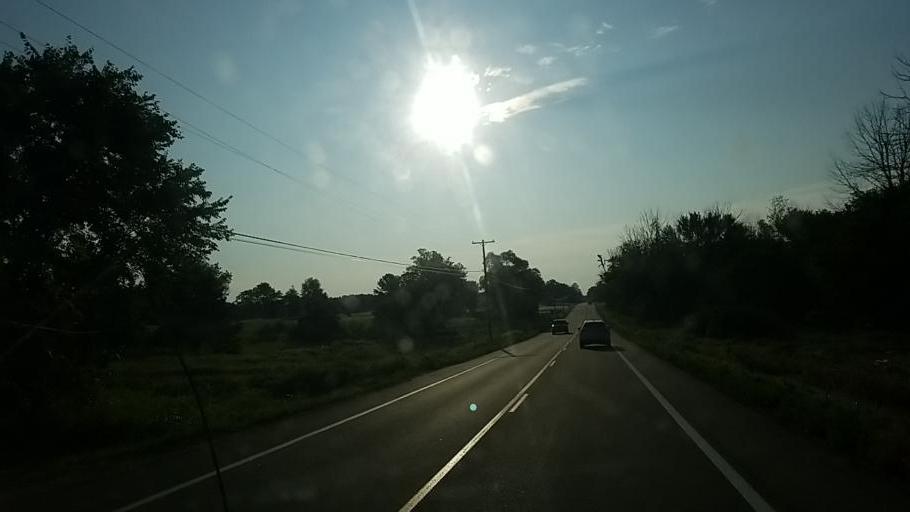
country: US
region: Michigan
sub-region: Montcalm County
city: Stanton
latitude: 43.2500
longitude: -85.1224
